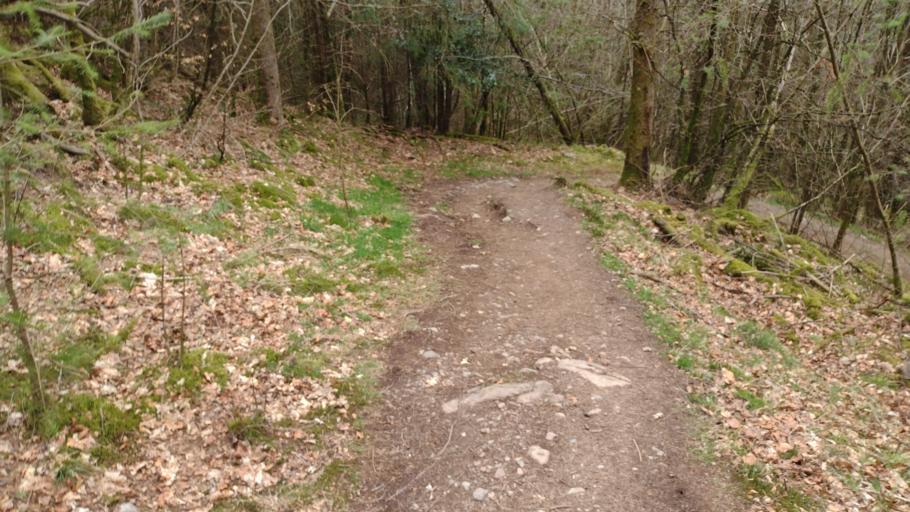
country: GB
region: England
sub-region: Cumbria
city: Keswick
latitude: 54.5620
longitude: -3.0780
